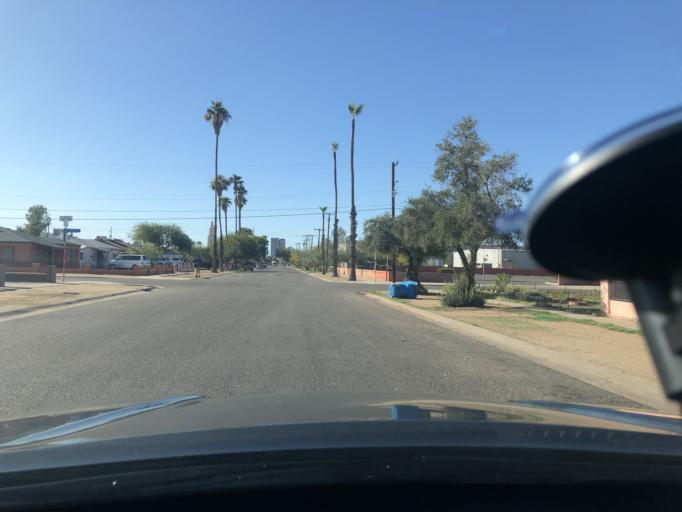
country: US
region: Arizona
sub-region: Maricopa County
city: Phoenix
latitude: 33.4647
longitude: -112.0407
